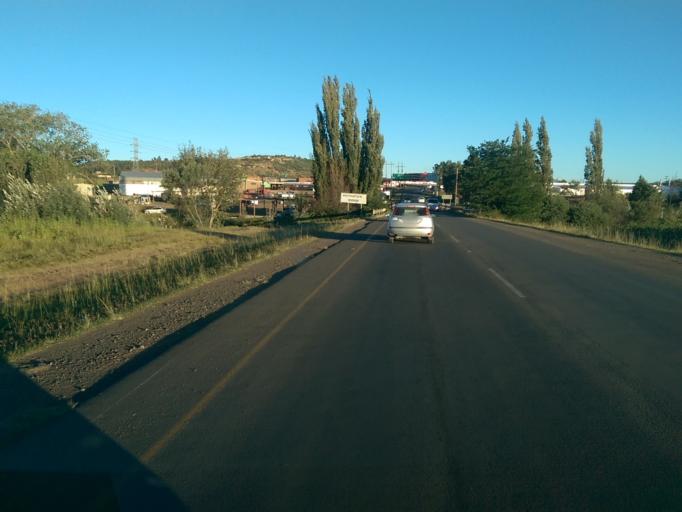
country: LS
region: Maseru
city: Maseru
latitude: -29.4024
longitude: 27.5584
